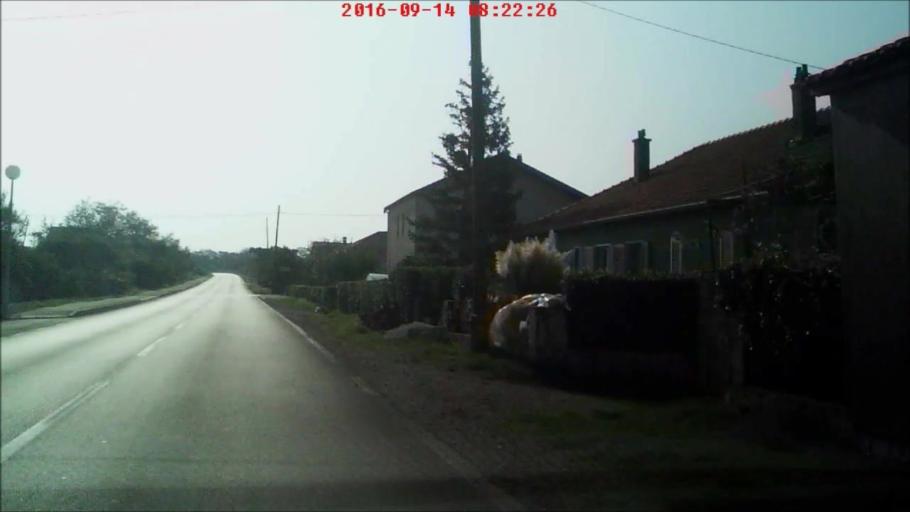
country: HR
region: Zadarska
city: Nin
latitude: 44.2177
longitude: 15.2189
